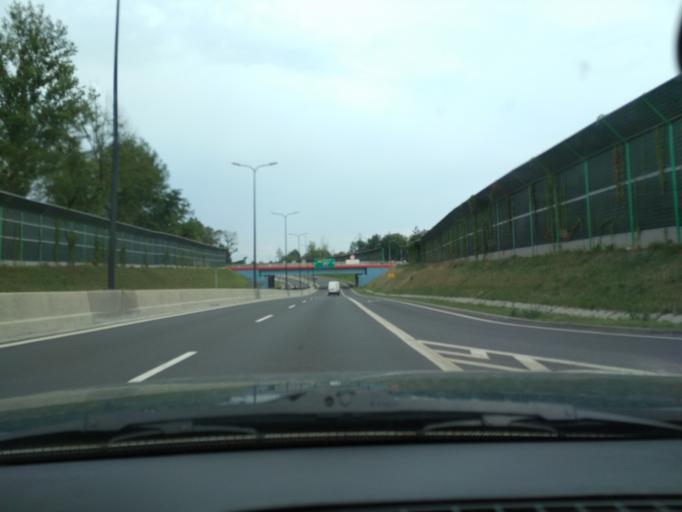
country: PL
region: Silesian Voivodeship
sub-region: Gliwice
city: Gliwice
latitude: 50.2927
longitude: 18.6881
